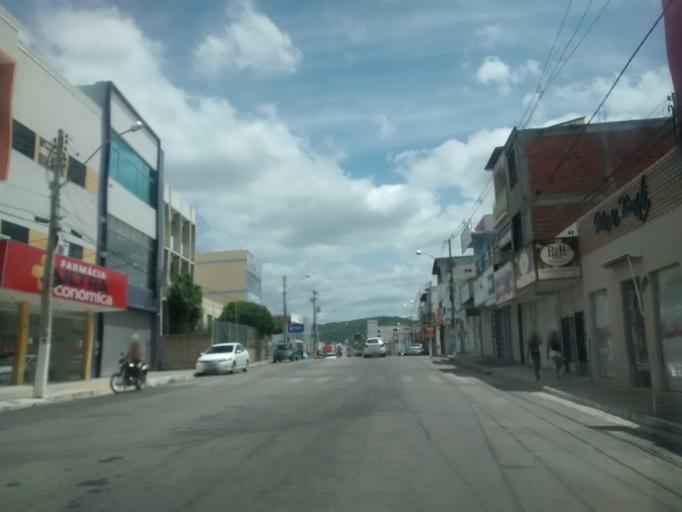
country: BR
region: Bahia
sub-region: Brumado
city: Brumado
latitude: -14.2069
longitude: -41.6659
